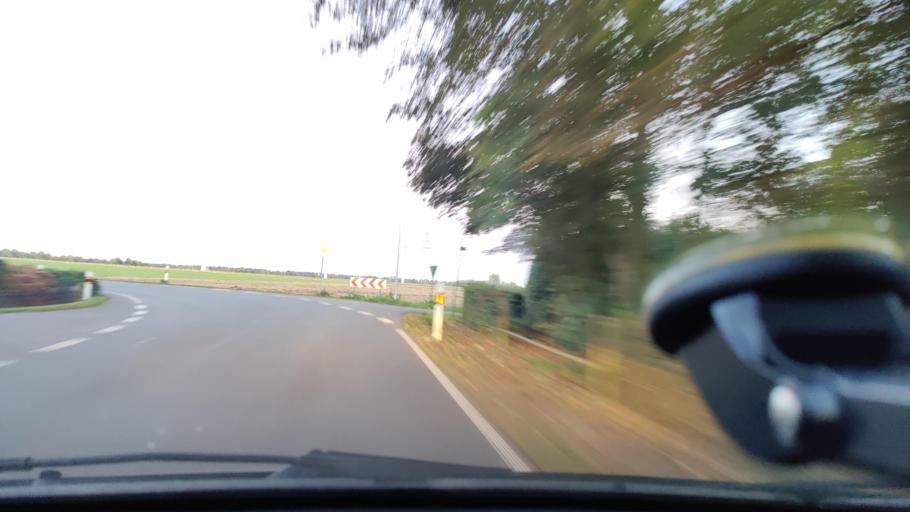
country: DE
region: North Rhine-Westphalia
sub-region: Regierungsbezirk Dusseldorf
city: Goch
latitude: 51.7169
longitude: 6.2084
